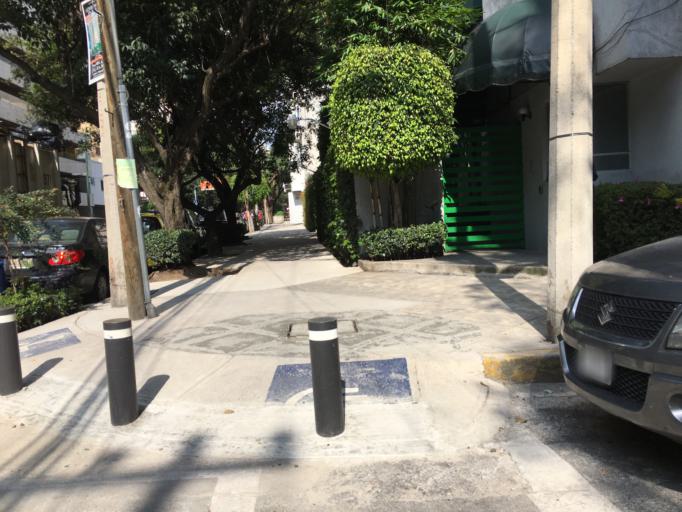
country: MX
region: Mexico City
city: Colonia del Valle
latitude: 19.3777
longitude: -99.1762
